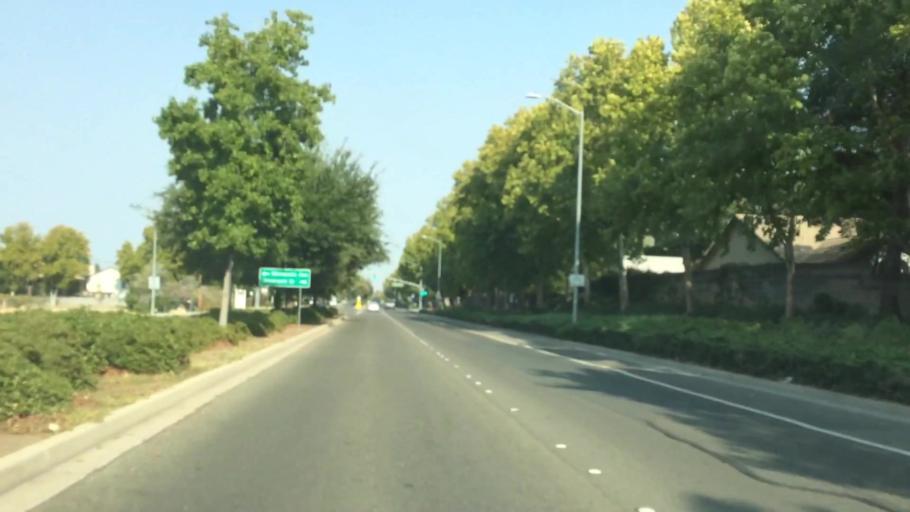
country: US
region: California
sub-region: Contra Costa County
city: Brentwood
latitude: 37.9253
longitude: -121.7163
